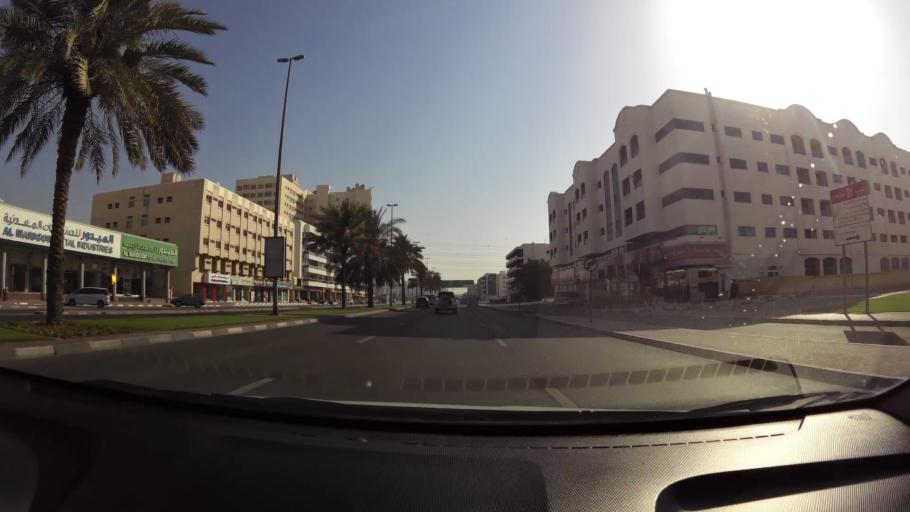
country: AE
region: Ash Shariqah
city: Sharjah
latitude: 25.2739
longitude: 55.3822
